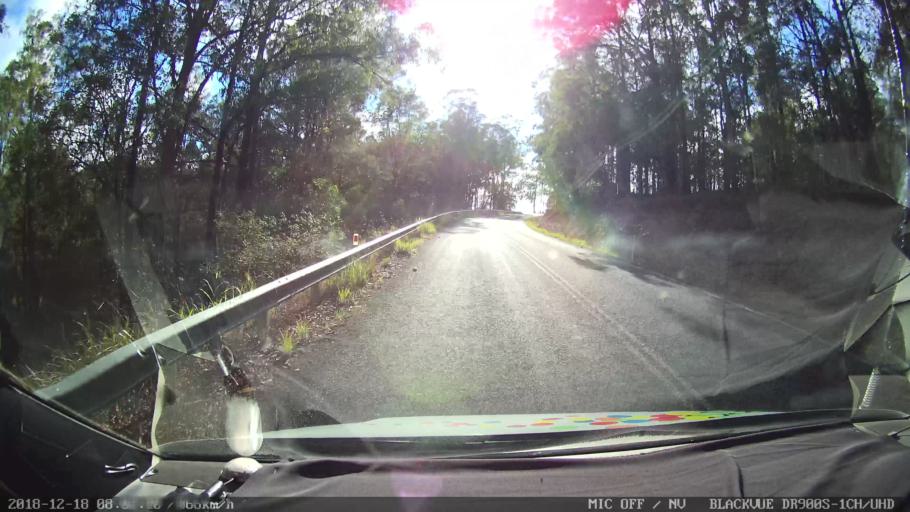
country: AU
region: New South Wales
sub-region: Kyogle
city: Kyogle
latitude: -28.3923
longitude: 152.6301
